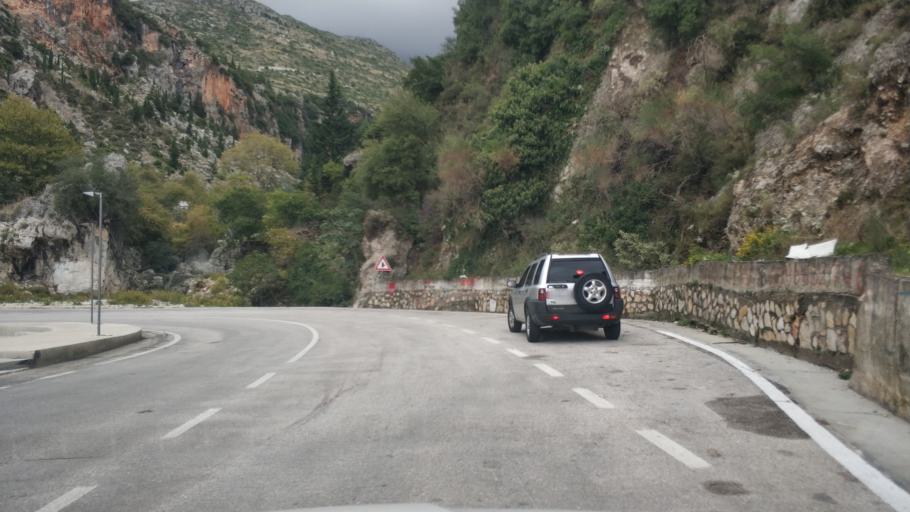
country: AL
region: Vlore
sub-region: Rrethi i Vlores
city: Vranisht
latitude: 40.1553
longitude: 19.6395
